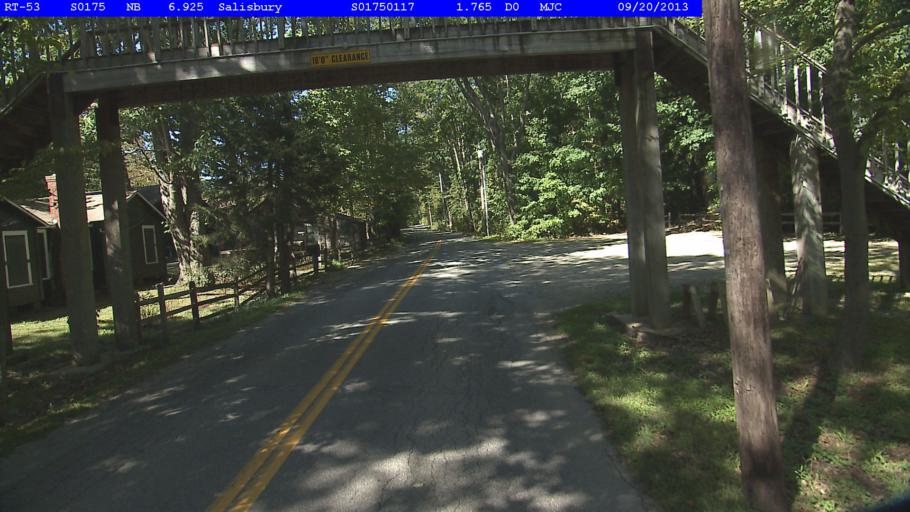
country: US
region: Vermont
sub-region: Rutland County
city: Brandon
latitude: 43.9218
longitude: -73.0728
